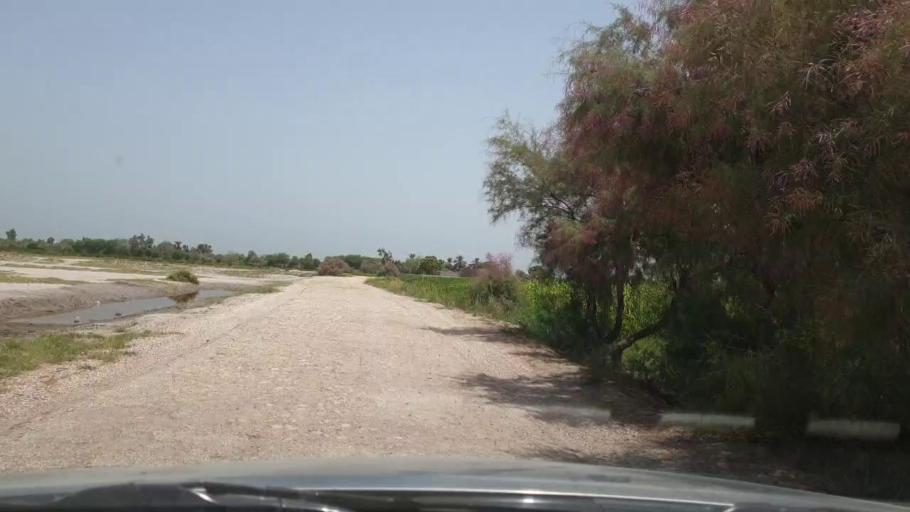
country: PK
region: Sindh
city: Pano Aqil
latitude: 27.8676
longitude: 69.1785
